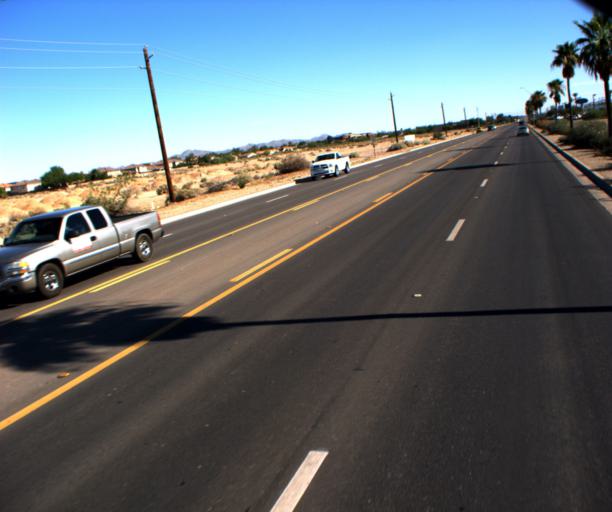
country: US
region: Arizona
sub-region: Pinal County
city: Casa Grande
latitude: 32.9030
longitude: -111.7572
